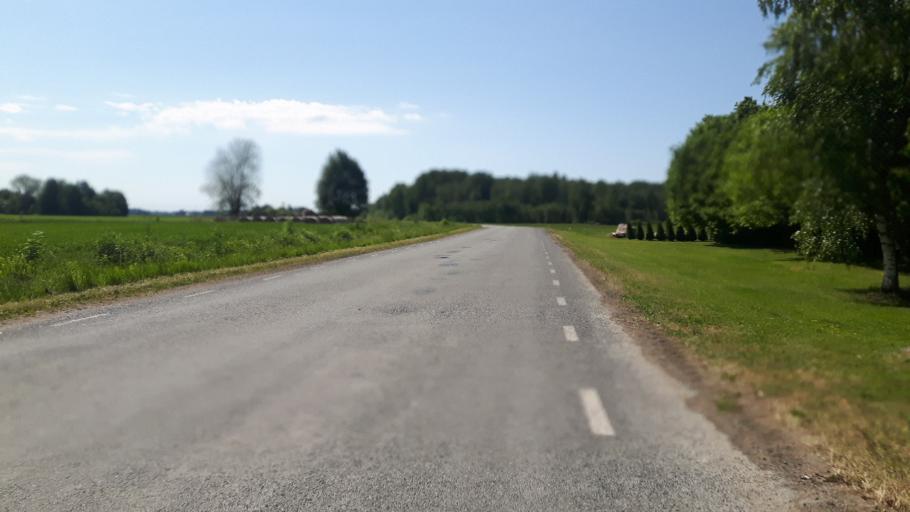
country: EE
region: Paernumaa
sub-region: Vaendra vald (alev)
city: Vandra
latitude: 58.6330
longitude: 25.0215
